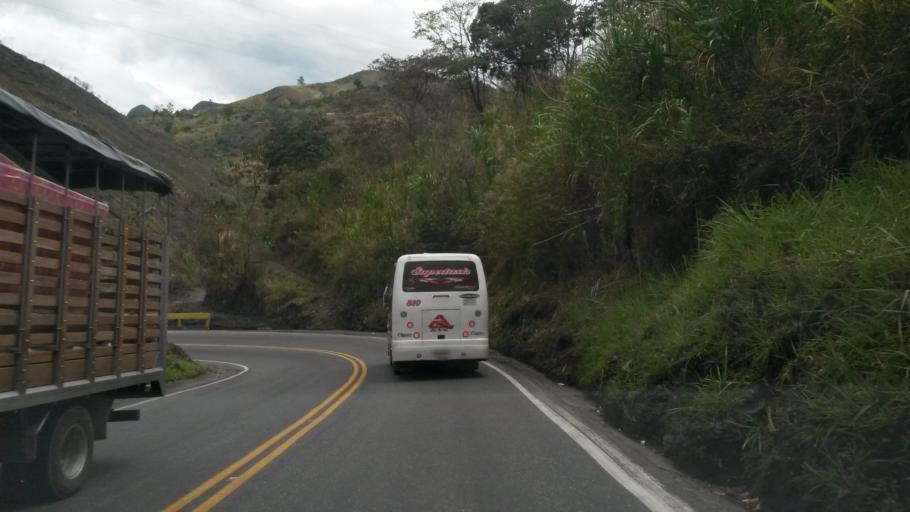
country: CO
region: Cauca
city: Rosas
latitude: 2.2762
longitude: -76.7098
